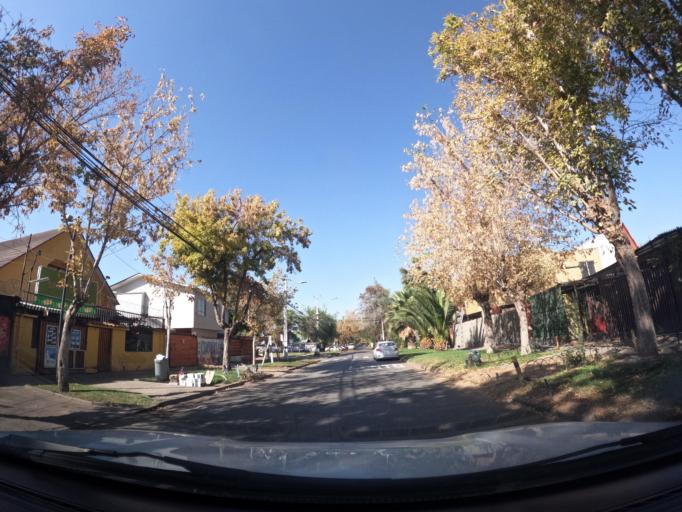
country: CL
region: Santiago Metropolitan
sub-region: Provincia de Santiago
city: Villa Presidente Frei, Nunoa, Santiago, Chile
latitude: -33.4680
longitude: -70.5696
